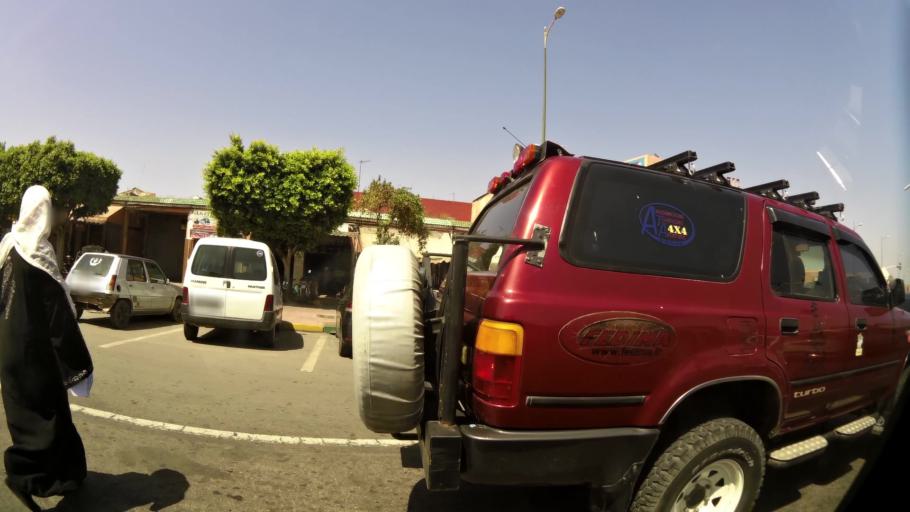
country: MA
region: Souss-Massa-Draa
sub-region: Inezgane-Ait Mellou
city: Inezgane
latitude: 30.3487
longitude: -9.5037
